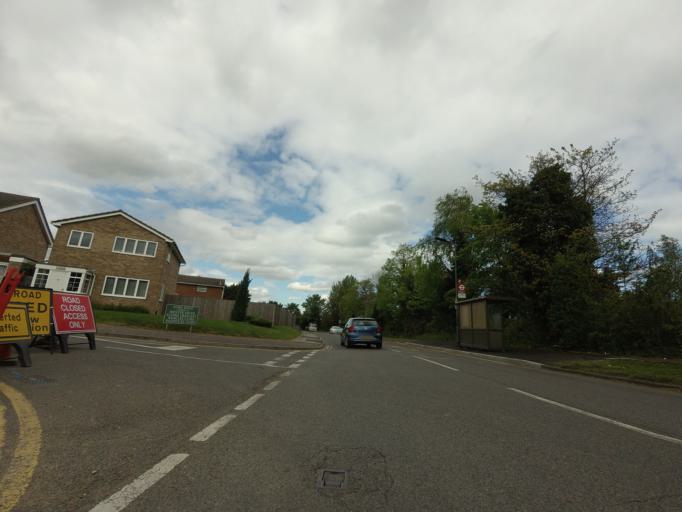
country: GB
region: England
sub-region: Greater London
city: Orpington
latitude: 51.3721
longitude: 0.1236
